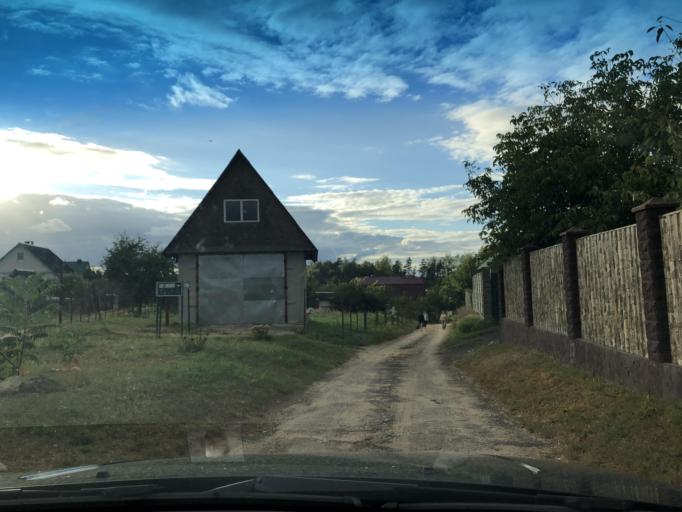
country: BY
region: Grodnenskaya
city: Hrodna
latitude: 53.7560
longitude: 23.8243
